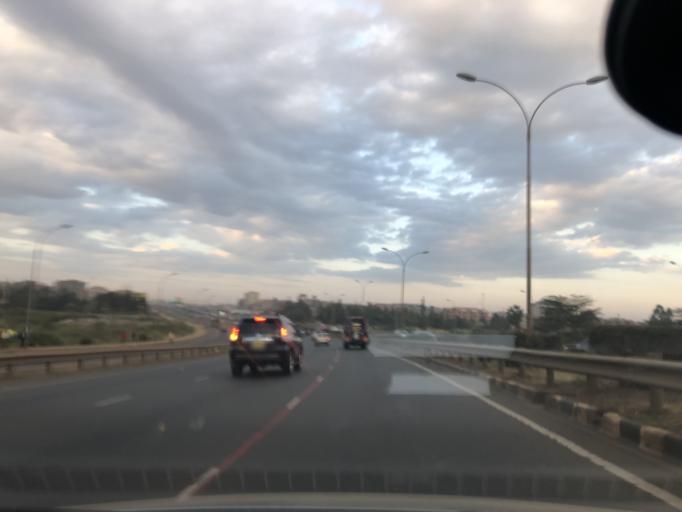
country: KE
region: Kiambu
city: Kiambu
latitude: -1.2100
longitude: 36.9102
